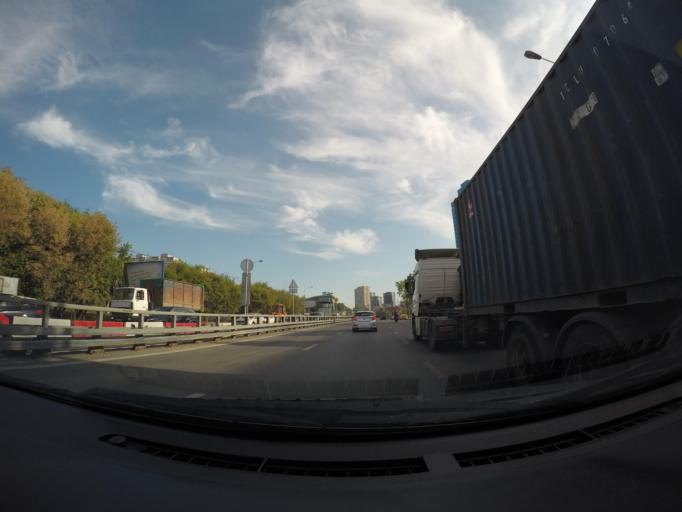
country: RU
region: Moscow
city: Likhobory
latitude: 55.8283
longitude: 37.5727
